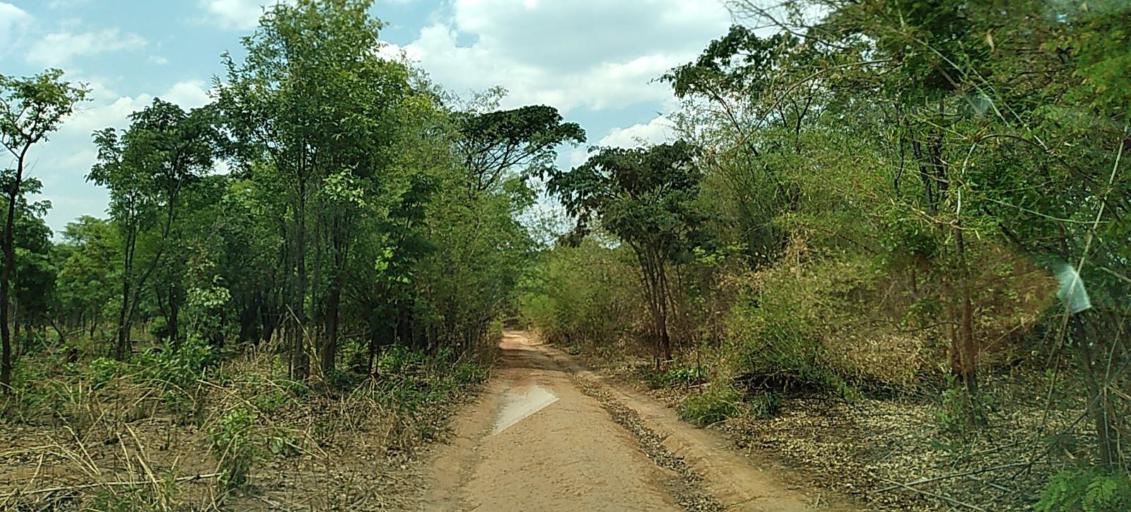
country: ZM
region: Copperbelt
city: Chililabombwe
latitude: -12.4755
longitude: 27.6495
